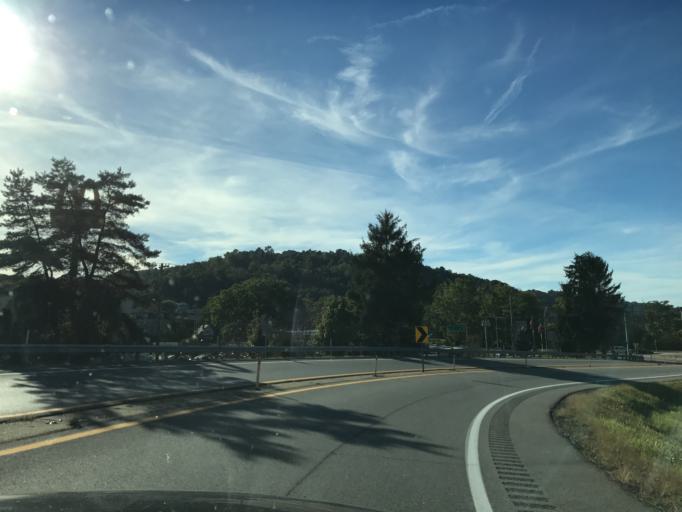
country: US
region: West Virginia
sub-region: Ohio County
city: Bethlehem
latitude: 40.0431
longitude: -80.6556
